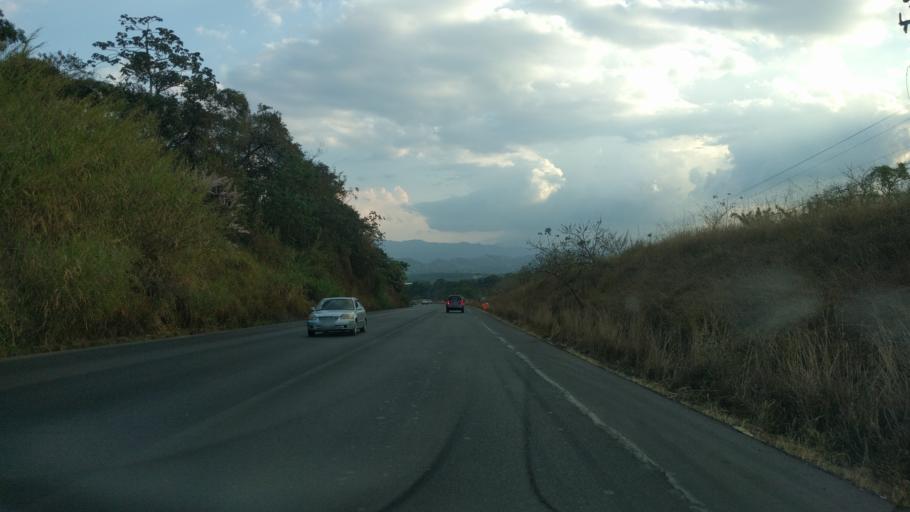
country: CR
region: Alajuela
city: Naranjo
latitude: 10.0447
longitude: -84.3622
